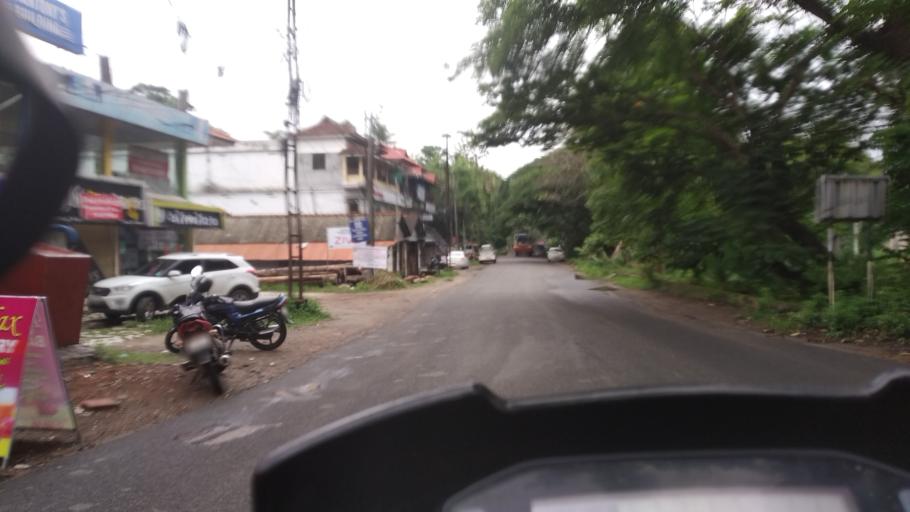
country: IN
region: Kerala
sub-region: Alappuzha
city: Alleppey
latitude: 9.4999
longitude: 76.3338
